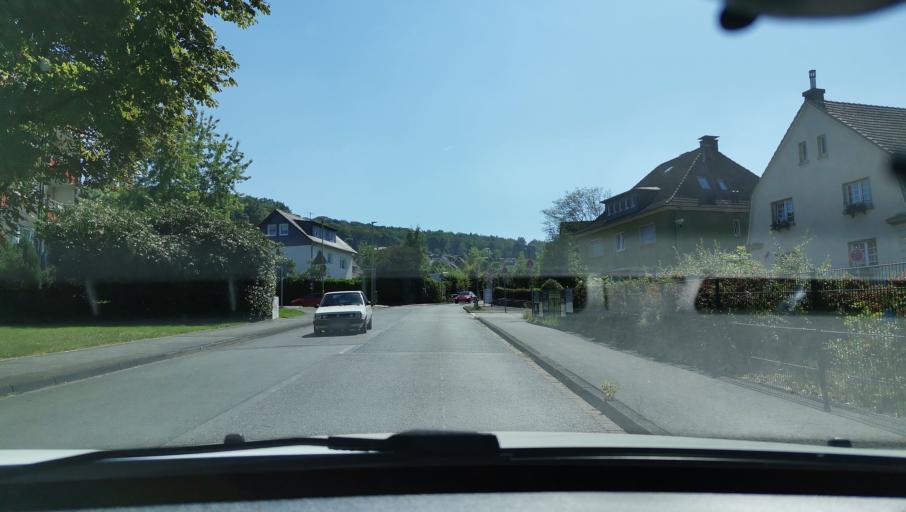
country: DE
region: North Rhine-Westphalia
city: Herdecke
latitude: 51.3799
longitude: 7.4375
